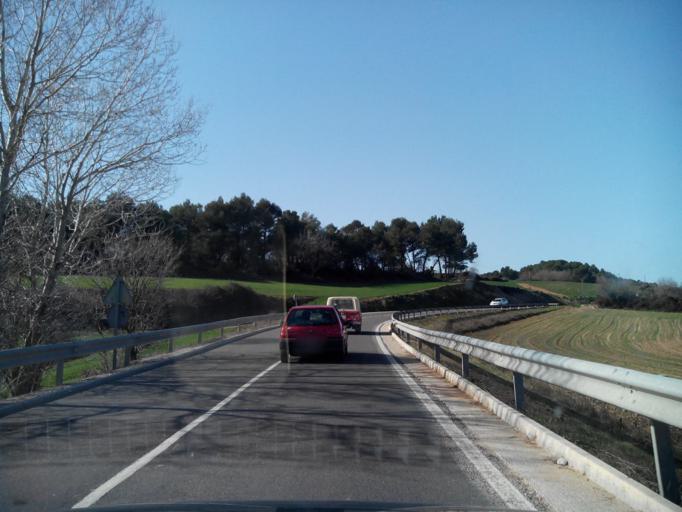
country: ES
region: Catalonia
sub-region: Provincia de Tarragona
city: Conesa
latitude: 41.4956
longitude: 1.3310
